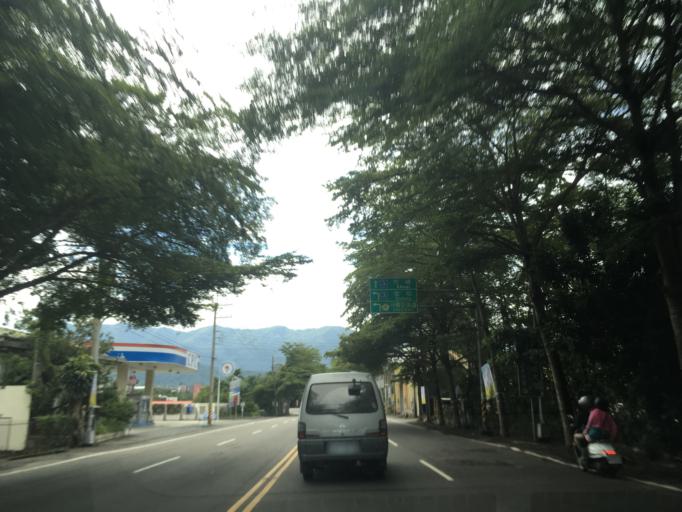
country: TW
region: Taiwan
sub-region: Yunlin
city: Douliu
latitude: 23.5911
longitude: 120.5364
